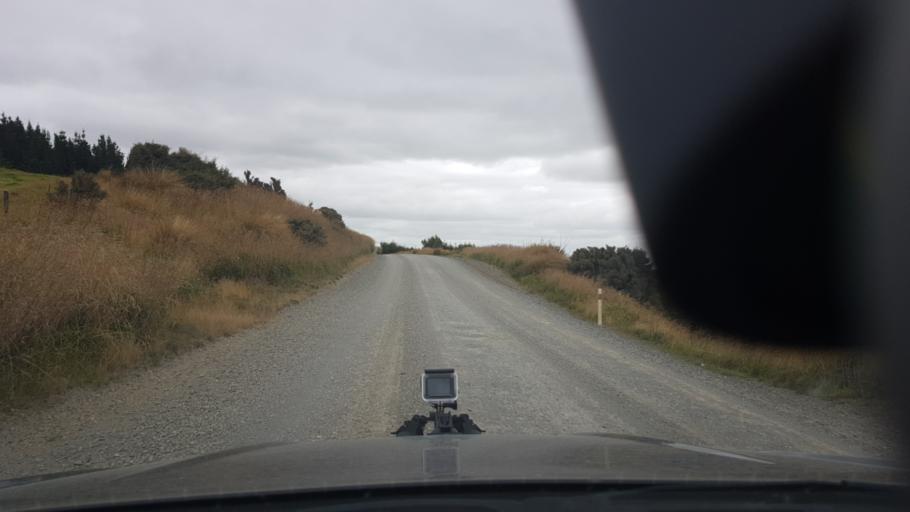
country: NZ
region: Otago
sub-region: Clutha District
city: Papatowai
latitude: -46.3271
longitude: 169.3913
